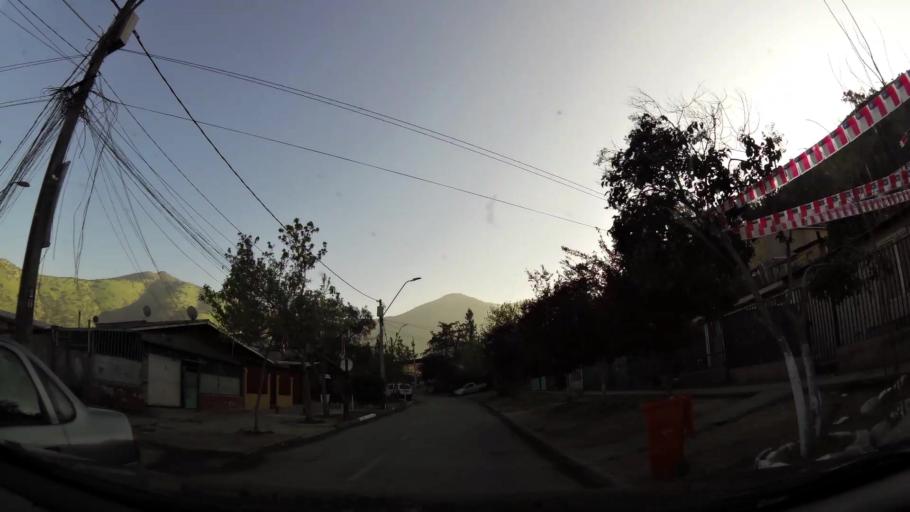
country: CL
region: Santiago Metropolitan
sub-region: Provincia de Chacabuco
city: Chicureo Abajo
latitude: -33.3675
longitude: -70.6292
